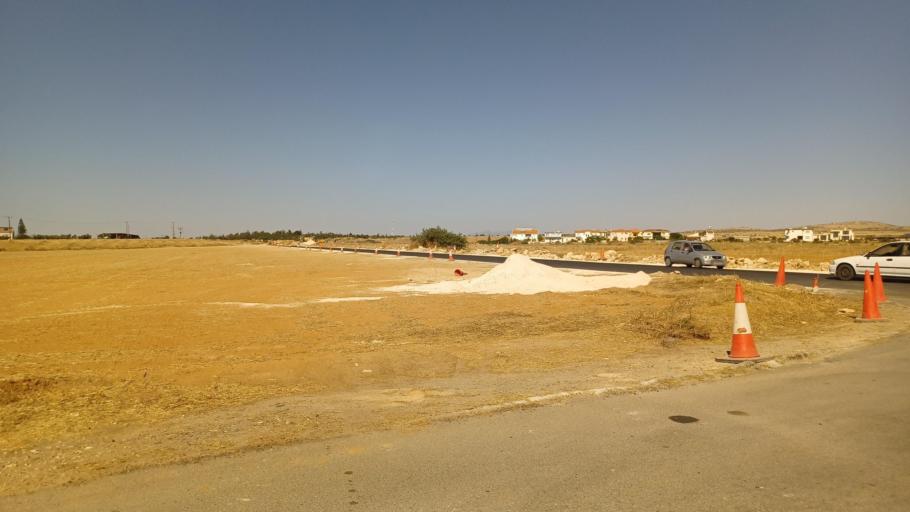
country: CY
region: Larnaka
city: Pyla
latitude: 35.0217
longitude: 33.7000
